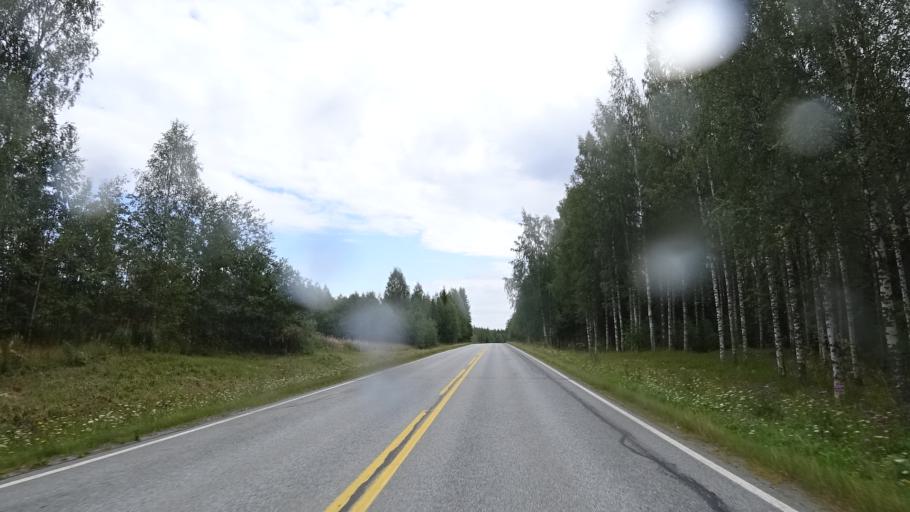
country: FI
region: North Karelia
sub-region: Keski-Karjala
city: Raeaekkylae
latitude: 62.1085
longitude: 29.7089
